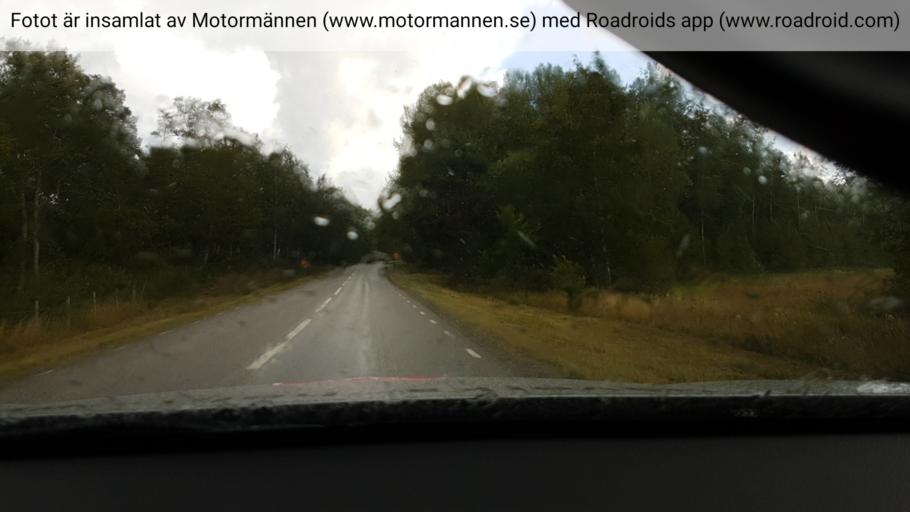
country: SE
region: Stockholm
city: Stenhamra
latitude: 59.3907
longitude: 17.5733
